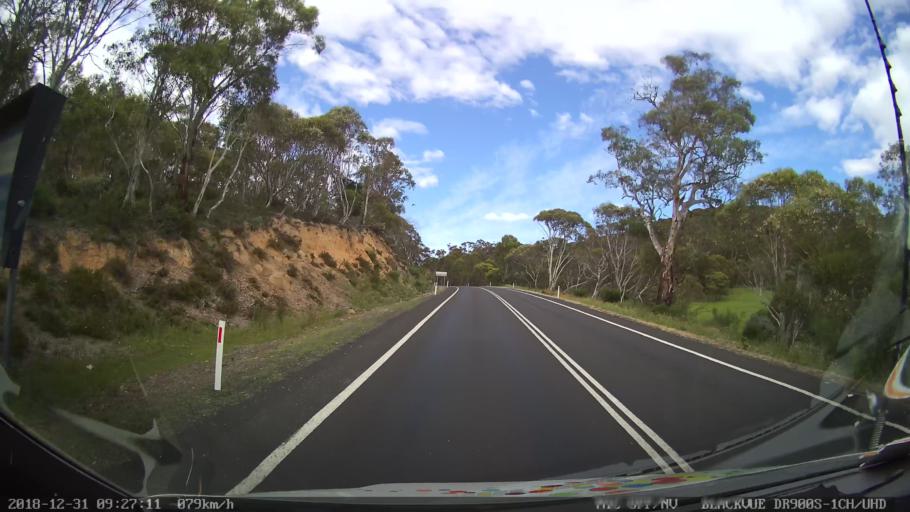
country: AU
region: New South Wales
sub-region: Snowy River
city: Jindabyne
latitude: -36.4547
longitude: 148.4879
